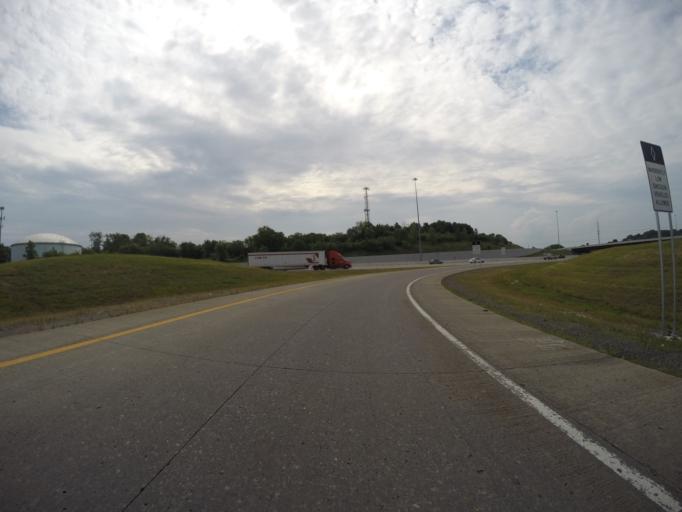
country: US
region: Tennessee
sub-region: Davidson County
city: Goodlettsville
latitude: 36.2666
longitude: -86.7383
